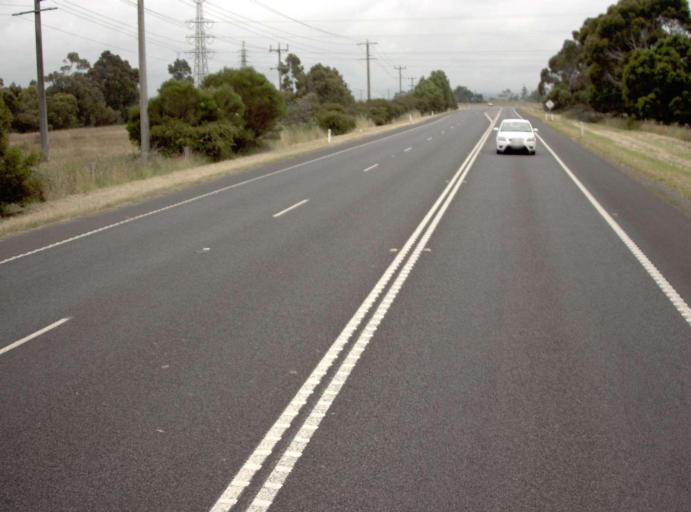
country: AU
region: Victoria
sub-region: Latrobe
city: Morwell
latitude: -38.2726
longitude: 146.4222
